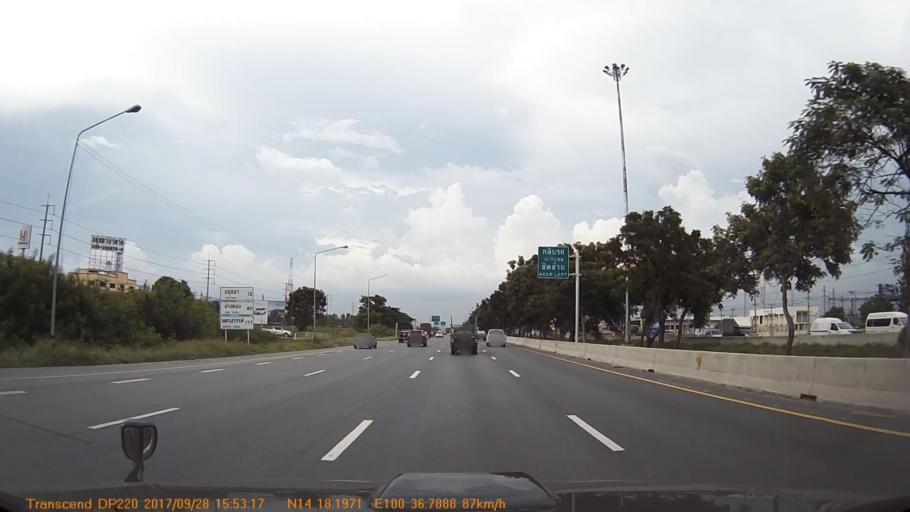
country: TH
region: Phra Nakhon Si Ayutthaya
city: Phra Nakhon Si Ayutthaya
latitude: 14.3035
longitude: 100.6131
